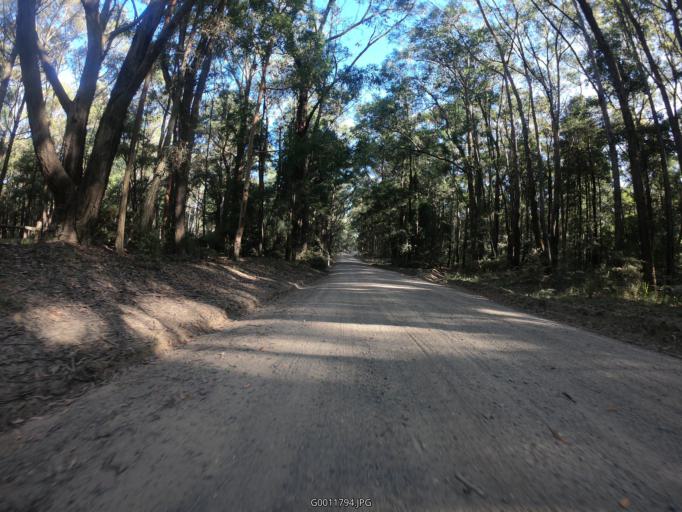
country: AU
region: New South Wales
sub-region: Lake Macquarie Shire
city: Cooranbong
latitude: -33.0628
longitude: 151.3317
